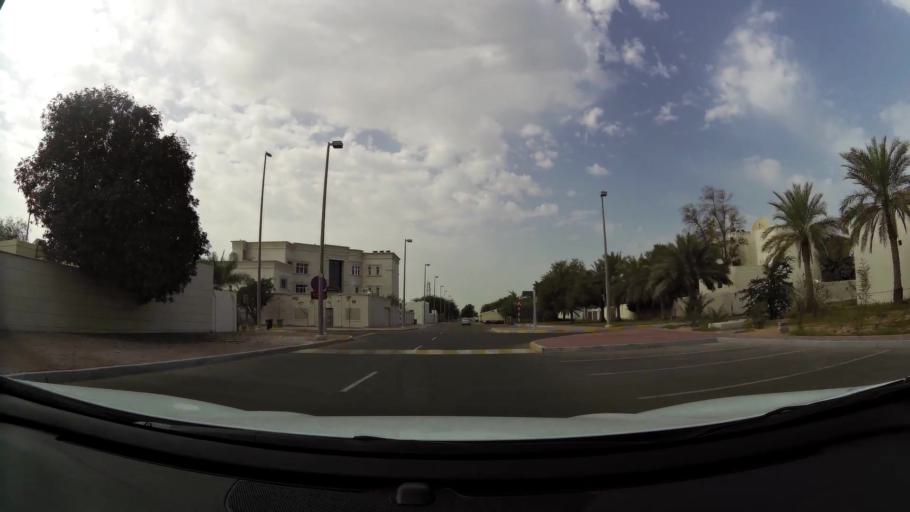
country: AE
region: Abu Dhabi
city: Abu Dhabi
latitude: 24.4383
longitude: 54.3719
